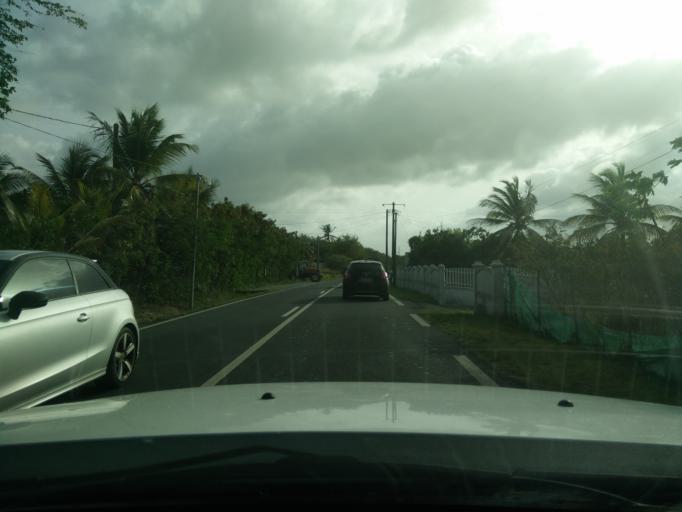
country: GP
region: Guadeloupe
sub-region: Guadeloupe
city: Saint-Francois
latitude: 16.2587
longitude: -61.2991
